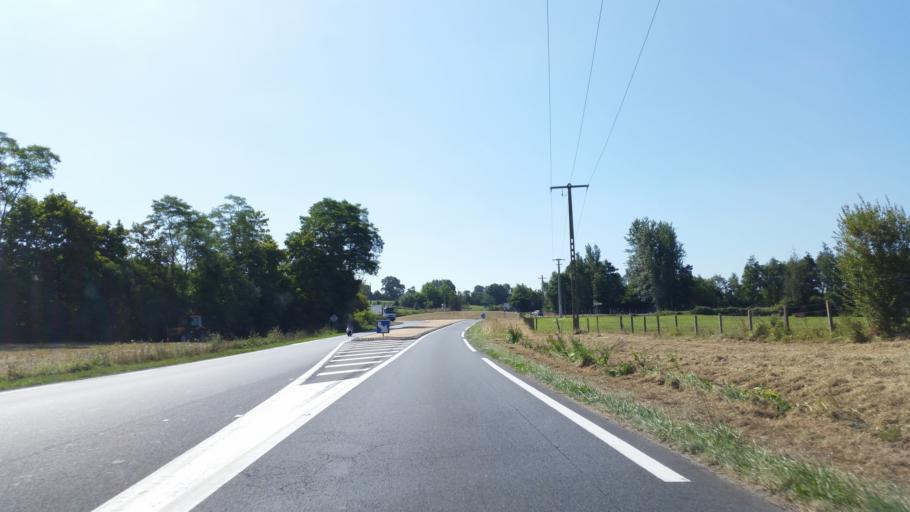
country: FR
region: Lower Normandy
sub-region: Departement du Calvados
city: Saint-Gatien-des-Bois
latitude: 49.2535
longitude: 0.2195
